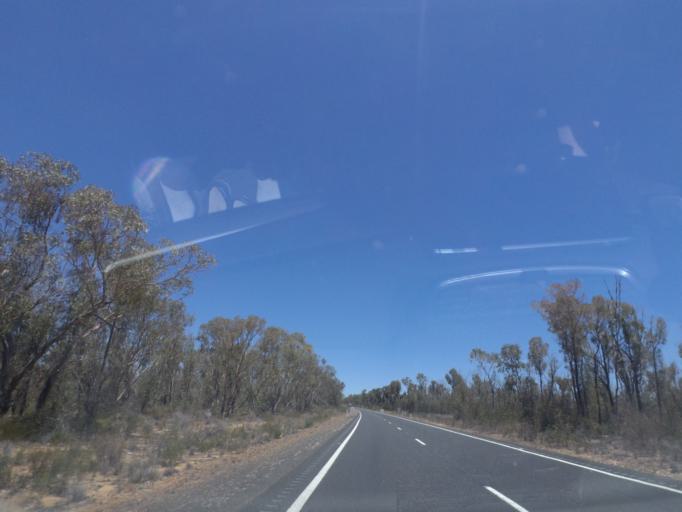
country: AU
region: New South Wales
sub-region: Warrumbungle Shire
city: Coonabarabran
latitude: -30.9440
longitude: 149.4227
